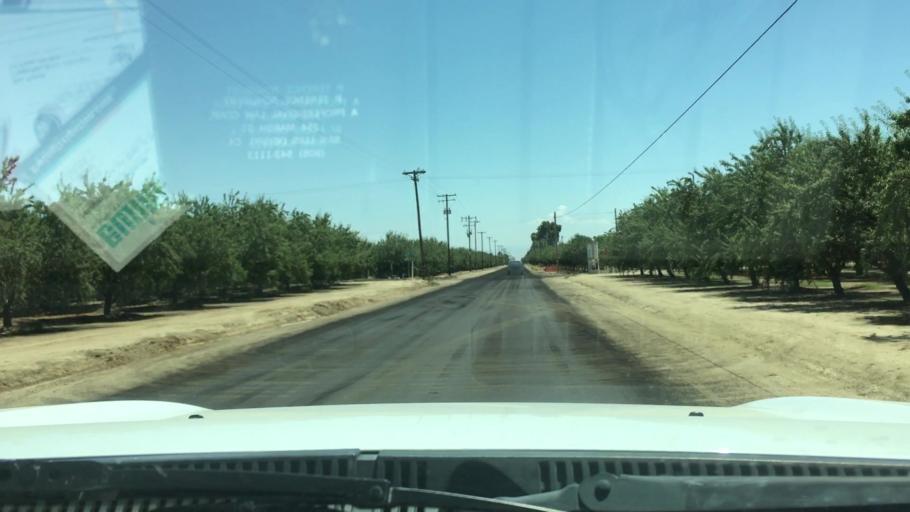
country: US
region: California
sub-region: Kern County
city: Wasco
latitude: 35.5290
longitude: -119.3331
